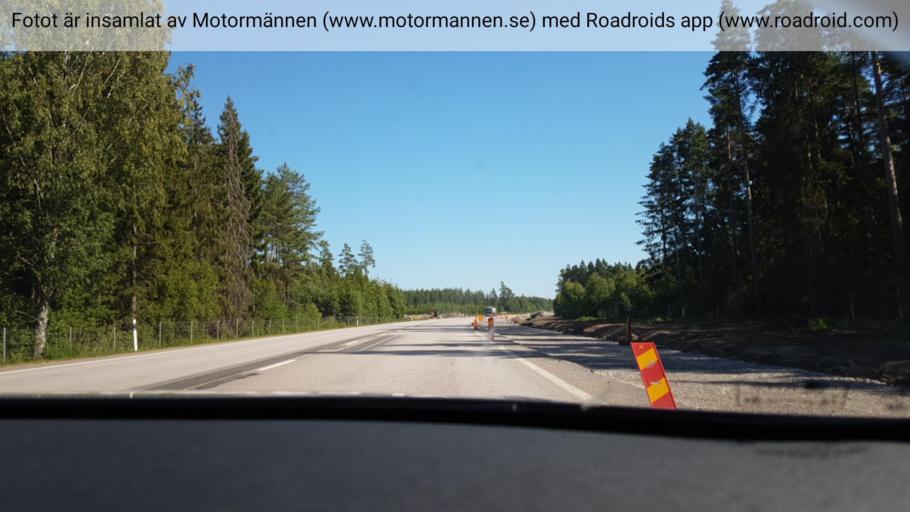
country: SE
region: Vaestra Goetaland
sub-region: Lidkopings Kommun
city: Lidkoping
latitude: 58.4818
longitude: 13.1985
